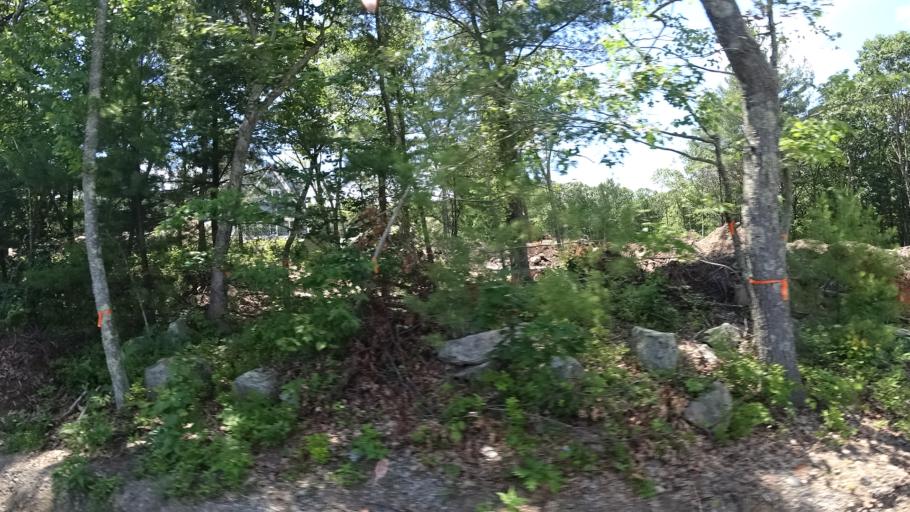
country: US
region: Massachusetts
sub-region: Norfolk County
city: Needham
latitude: 42.2582
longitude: -71.2138
